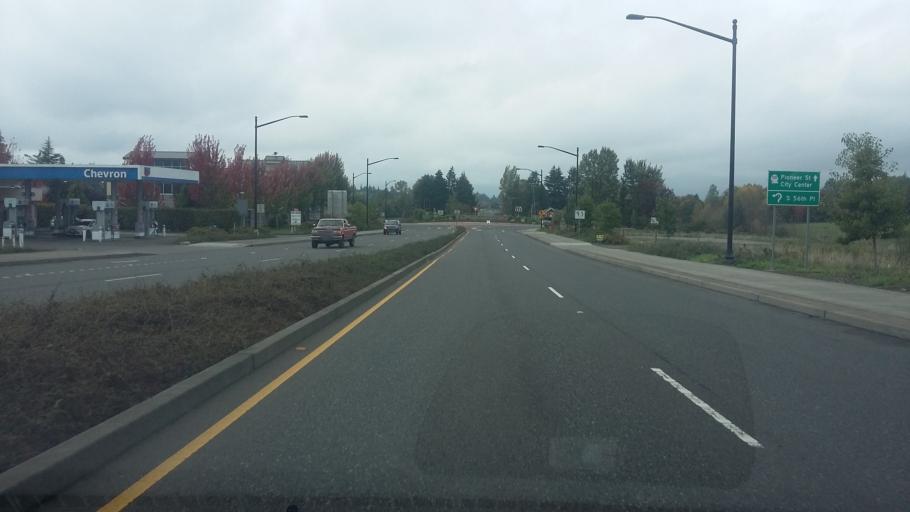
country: US
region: Washington
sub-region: Clark County
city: La Center
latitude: 45.8159
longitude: -122.6882
